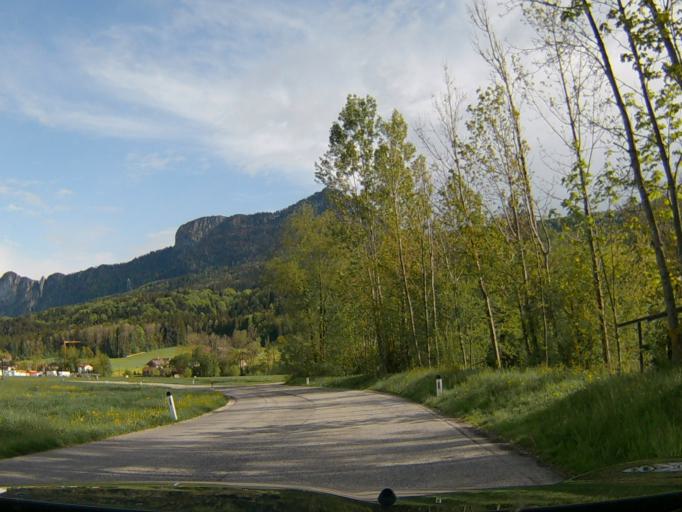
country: AT
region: Salzburg
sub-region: Politischer Bezirk Salzburg-Umgebung
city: Fuschl am See
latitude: 47.8383
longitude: 13.3011
